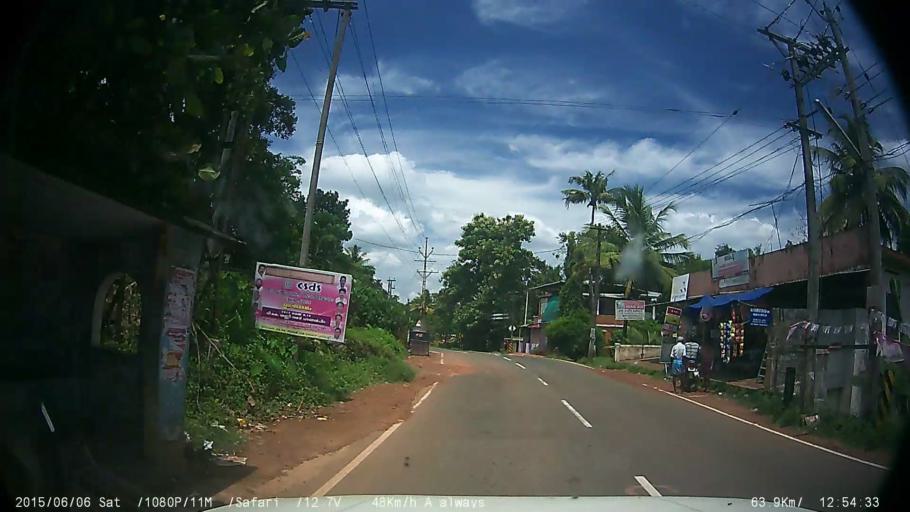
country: IN
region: Kerala
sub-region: Kottayam
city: Changanacheri
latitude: 9.5126
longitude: 76.5690
